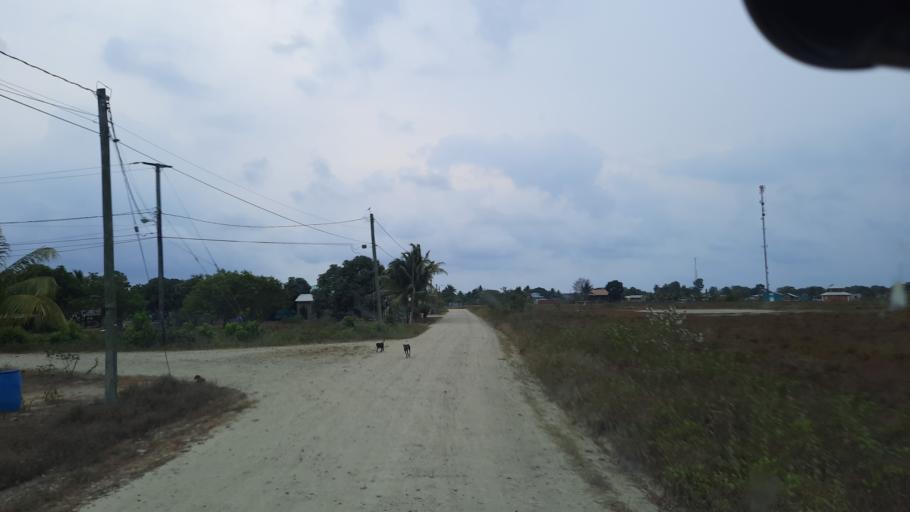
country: BZ
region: Stann Creek
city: Placencia
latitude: 16.5321
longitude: -88.4257
